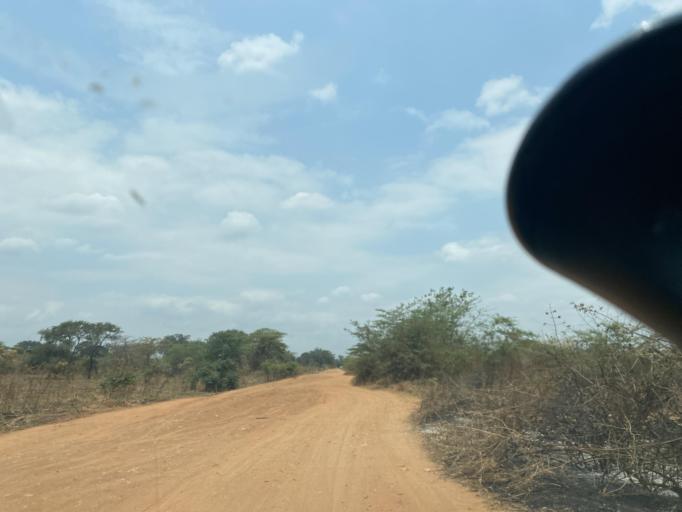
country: ZM
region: Lusaka
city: Chongwe
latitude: -15.5168
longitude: 28.8200
